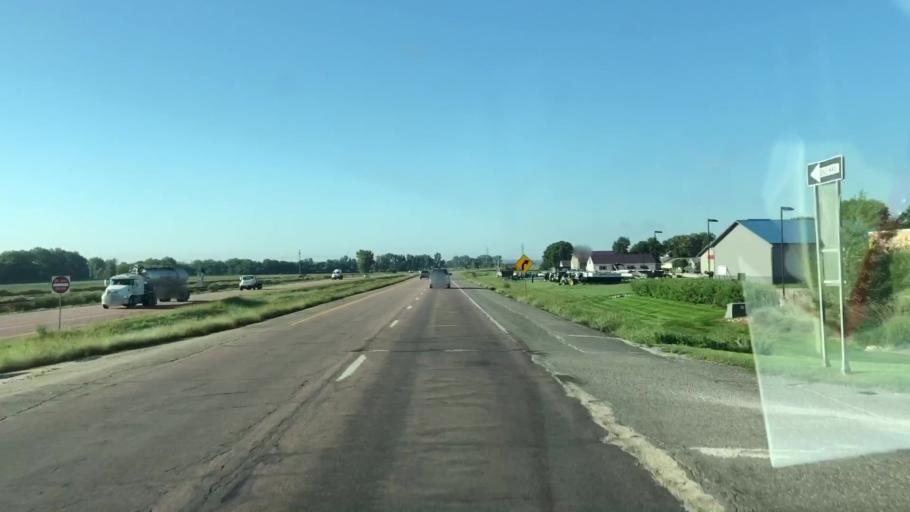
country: US
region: Iowa
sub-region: Woodbury County
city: Sioux City
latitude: 42.6168
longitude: -96.2950
